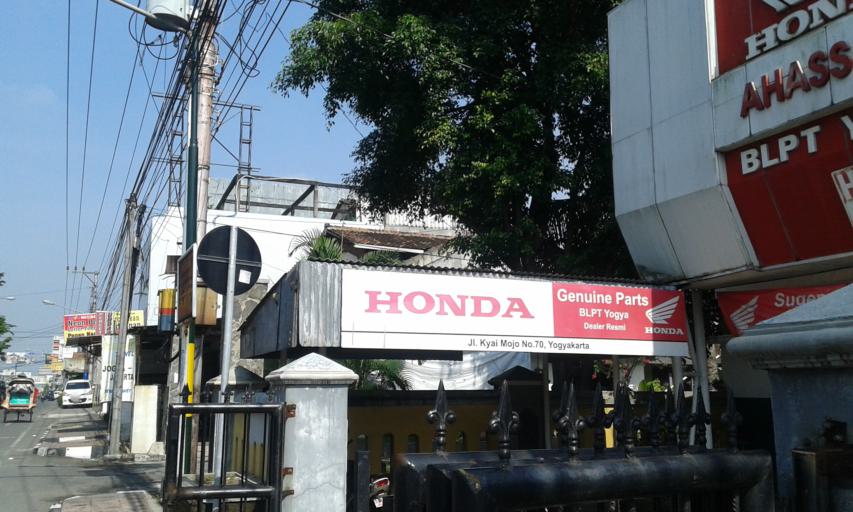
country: ID
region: Daerah Istimewa Yogyakarta
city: Yogyakarta
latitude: -7.7818
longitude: 110.3537
